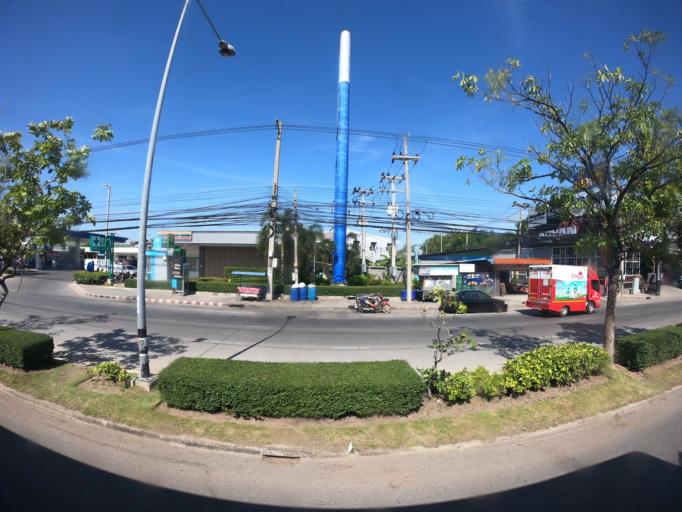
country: TH
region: Nakhon Ratchasima
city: Nakhon Ratchasima
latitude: 14.9900
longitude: 102.0970
